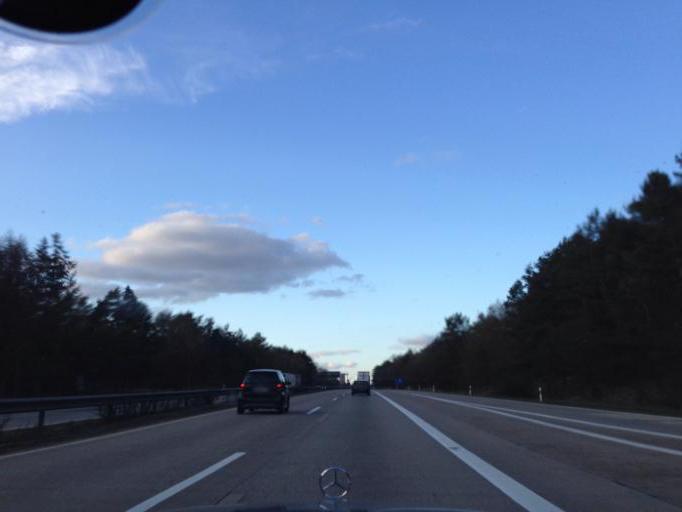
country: DE
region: Lower Saxony
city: Bad Fallingbostel
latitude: 52.7955
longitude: 9.6750
